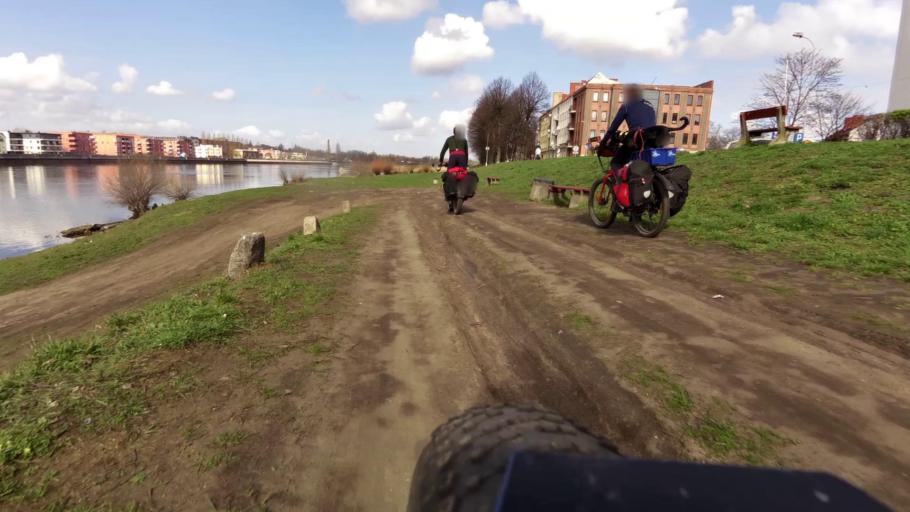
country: PL
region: Lubusz
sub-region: Powiat slubicki
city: Slubice
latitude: 52.3496
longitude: 14.5568
